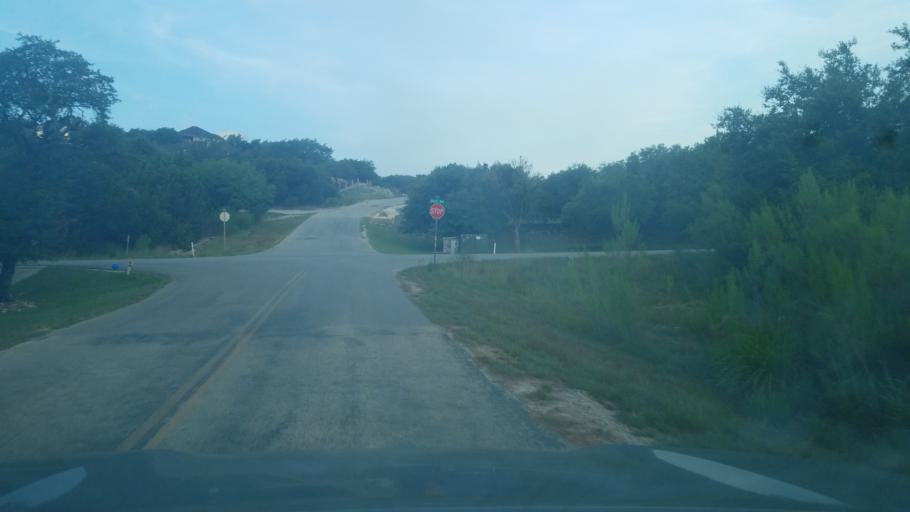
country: US
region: Texas
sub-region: Comal County
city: Bulverde
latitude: 29.8164
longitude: -98.4067
